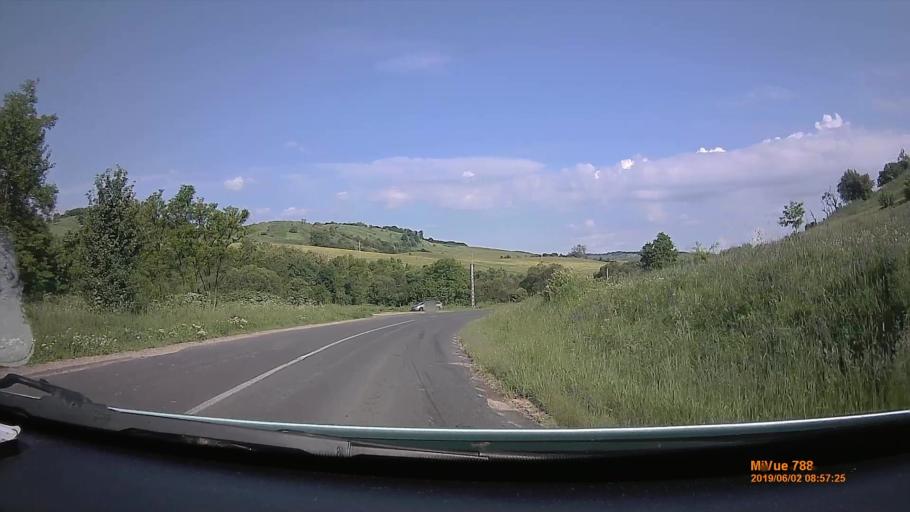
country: HU
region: Borsod-Abauj-Zemplen
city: Sajobabony
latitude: 48.1559
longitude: 20.6400
